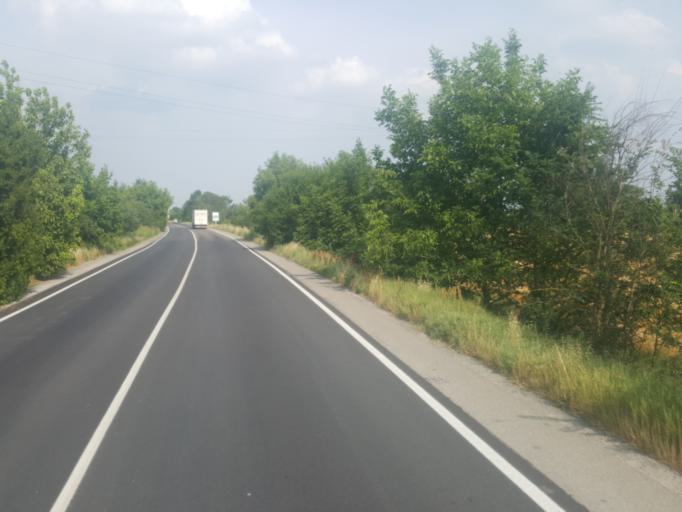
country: IT
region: Emilia-Romagna
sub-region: Provincia di Modena
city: Castelfranco Emilia
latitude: 44.5809
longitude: 11.0600
